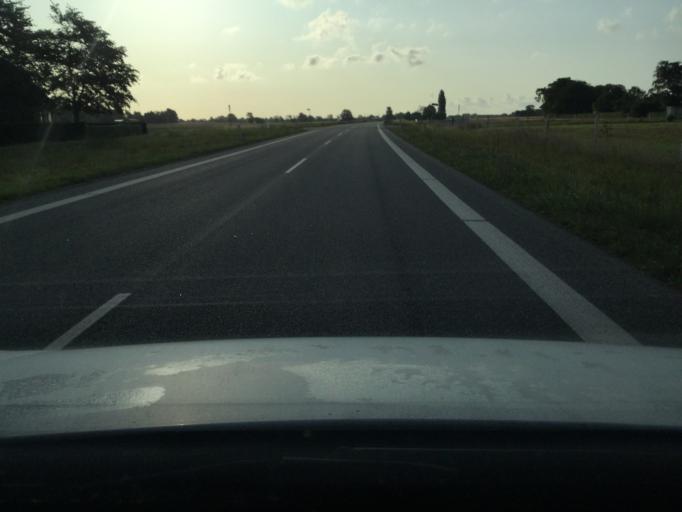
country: DK
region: Zealand
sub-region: Lolland Kommune
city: Rodby
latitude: 54.7542
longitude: 11.3621
